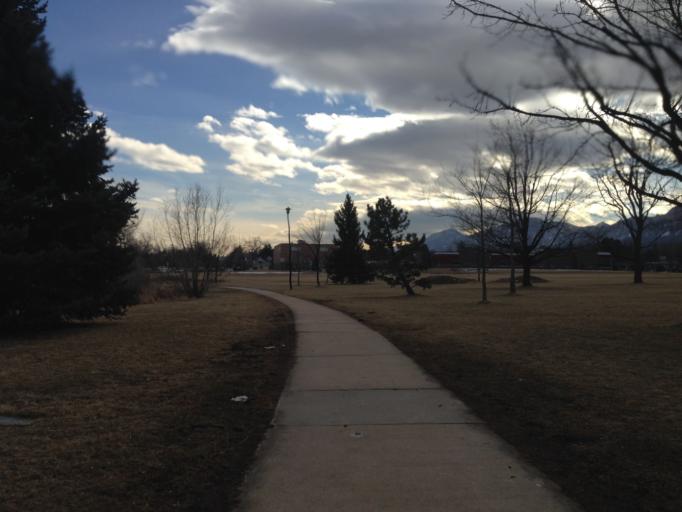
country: US
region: Colorado
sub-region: Boulder County
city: Boulder
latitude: 39.9959
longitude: -105.2365
